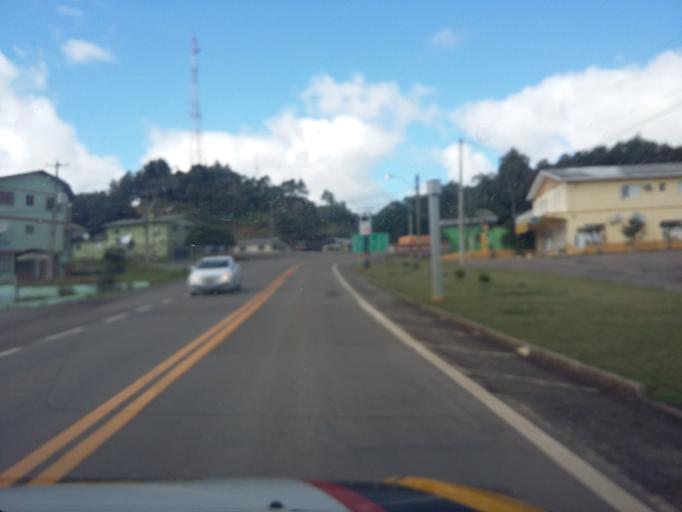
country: BR
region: Rio Grande do Sul
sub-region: Sao Marcos
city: Sao Marcos
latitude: -28.7942
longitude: -51.0957
